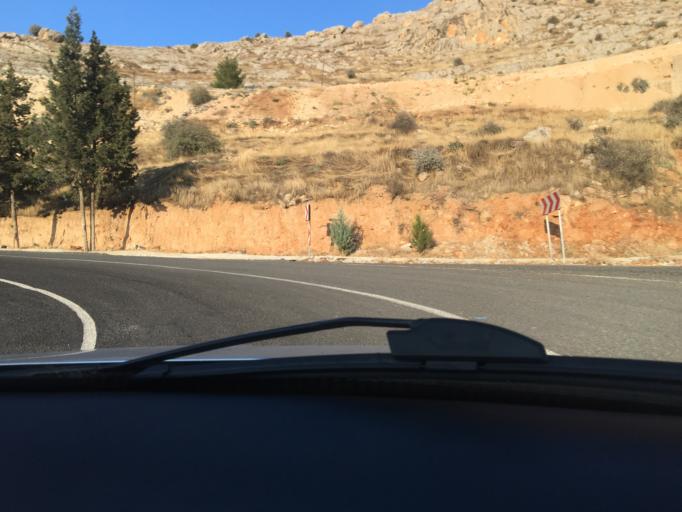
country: TR
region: Sanliurfa
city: Halfeti
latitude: 37.2438
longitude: 37.8740
